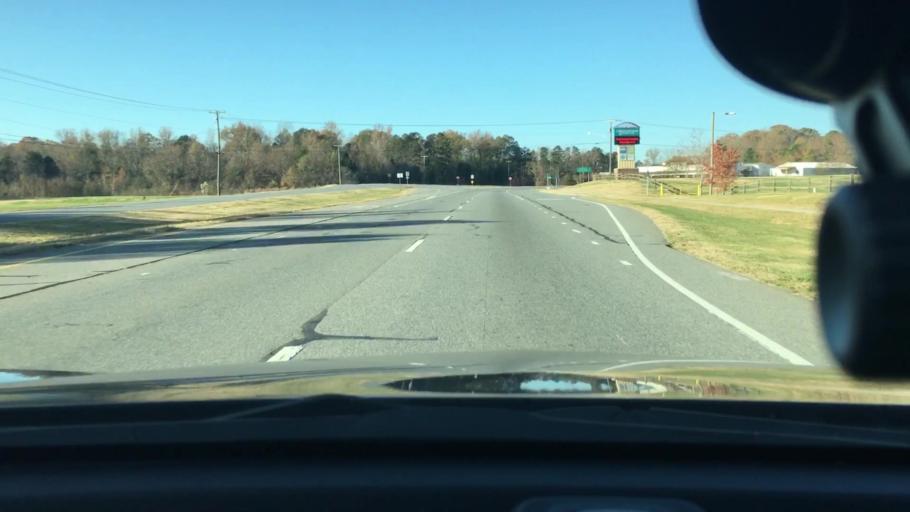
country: US
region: North Carolina
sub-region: Cabarrus County
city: Mount Pleasant
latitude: 35.3876
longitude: -80.4972
